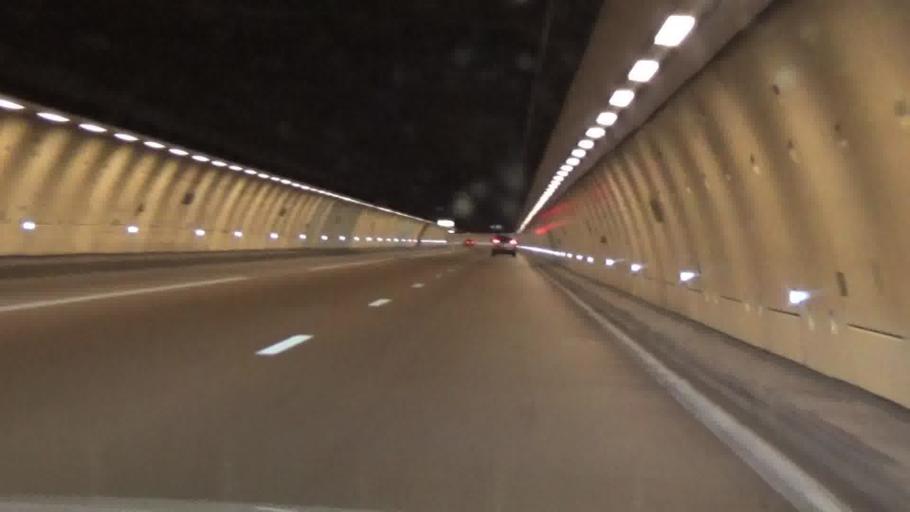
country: FR
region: Ile-de-France
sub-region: Departement des Yvelines
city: La Celle-Saint-Cloud
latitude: 48.8528
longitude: 2.1533
